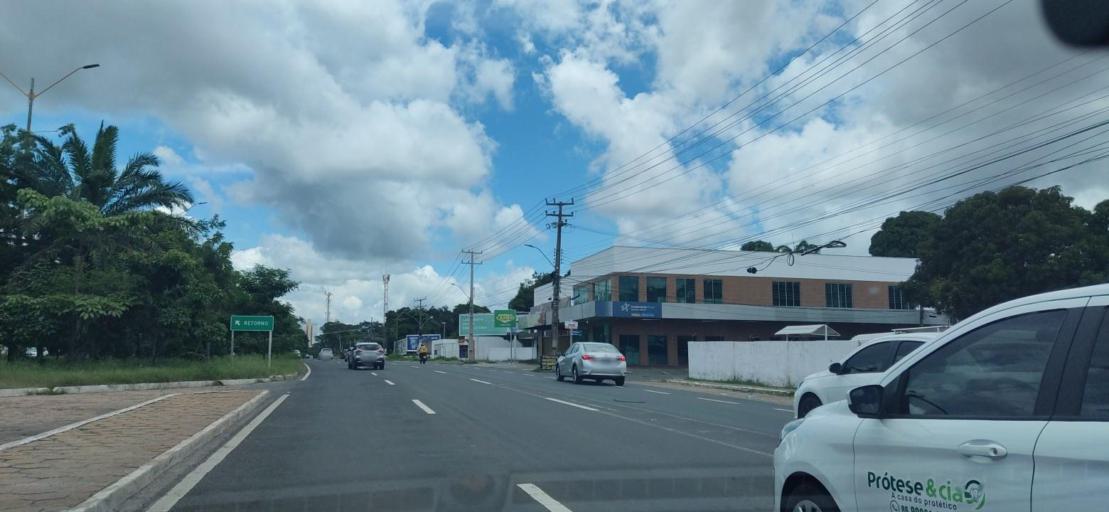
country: BR
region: Piaui
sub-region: Teresina
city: Teresina
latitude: -5.0816
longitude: -42.7737
